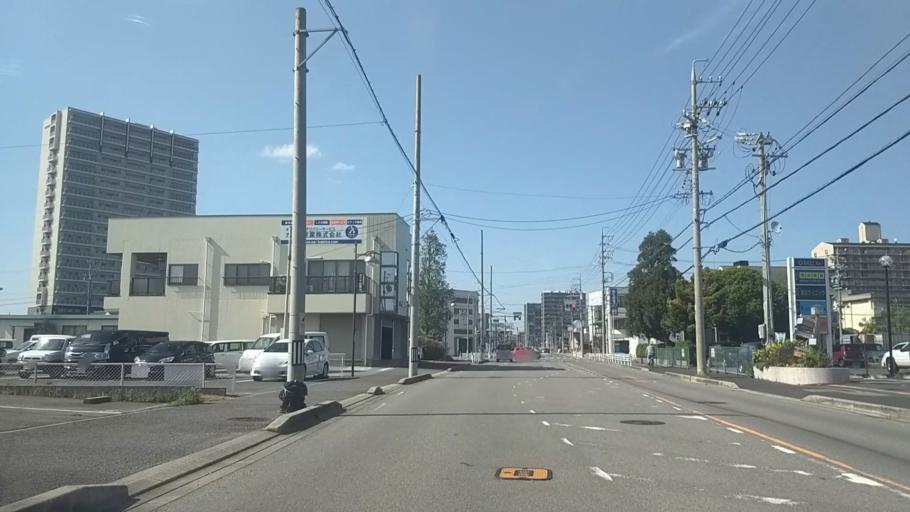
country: JP
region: Aichi
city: Anjo
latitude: 34.9804
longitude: 137.0844
